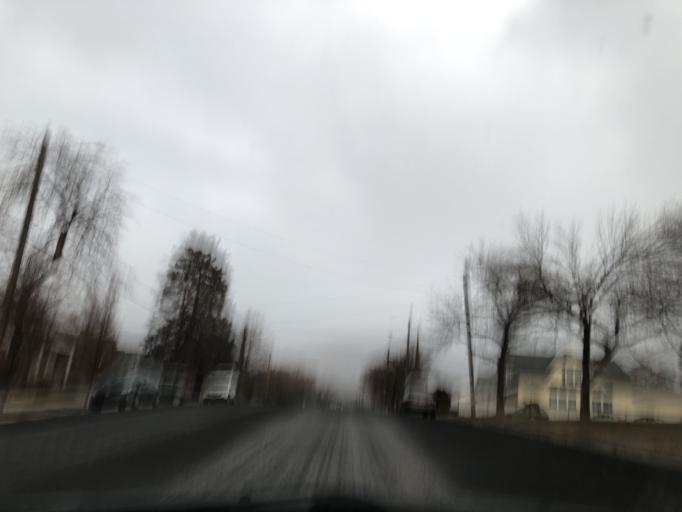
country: US
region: Utah
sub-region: Cache County
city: Logan
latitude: 41.7369
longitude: -111.8241
